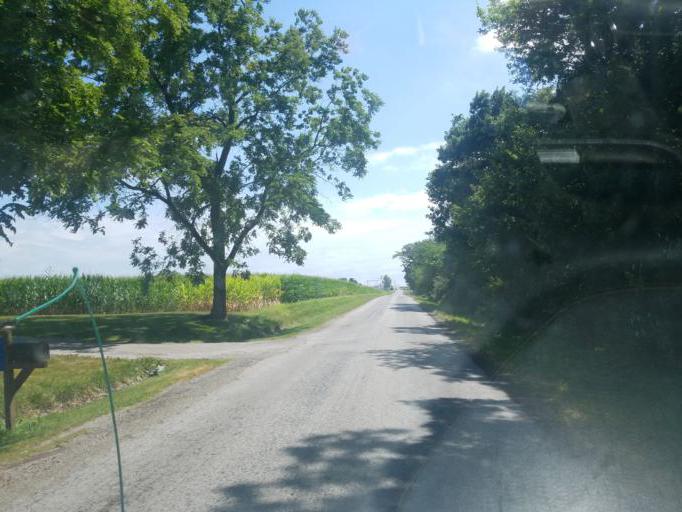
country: US
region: Indiana
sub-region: Allen County
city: Harlan
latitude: 41.1890
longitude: -84.8840
